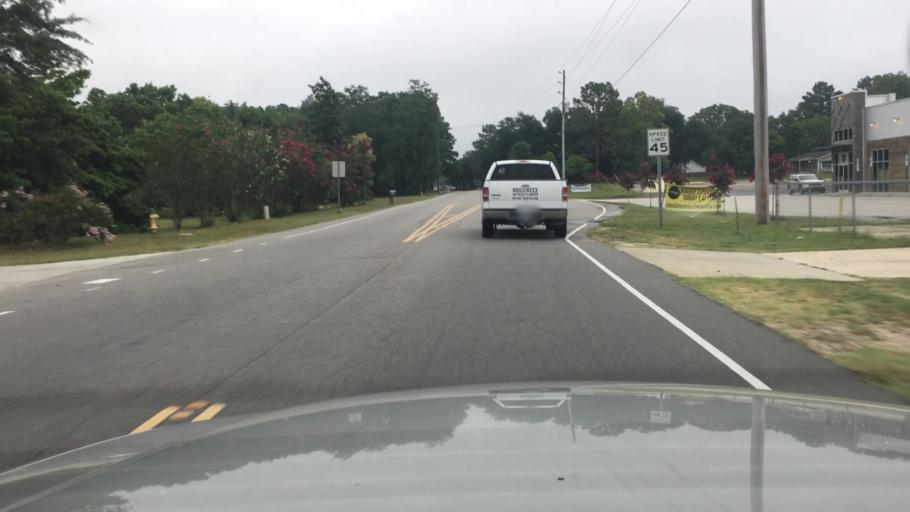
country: US
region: North Carolina
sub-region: Cumberland County
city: Hope Mills
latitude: 34.9754
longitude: -78.9974
